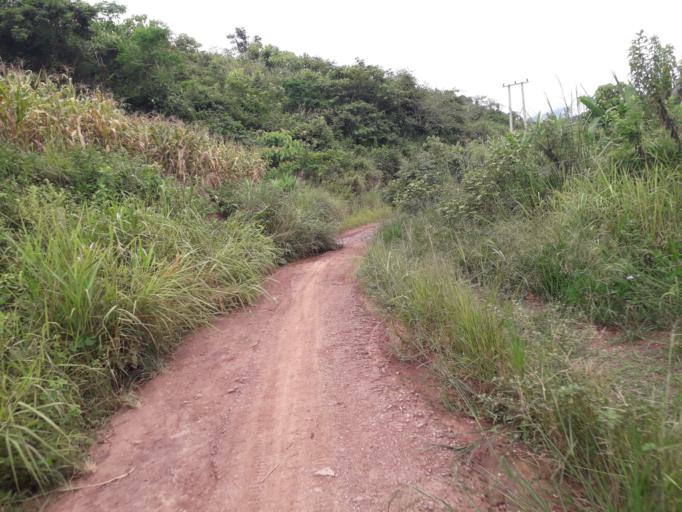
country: CN
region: Yunnan
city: Menglie
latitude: 22.2572
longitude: 101.5981
